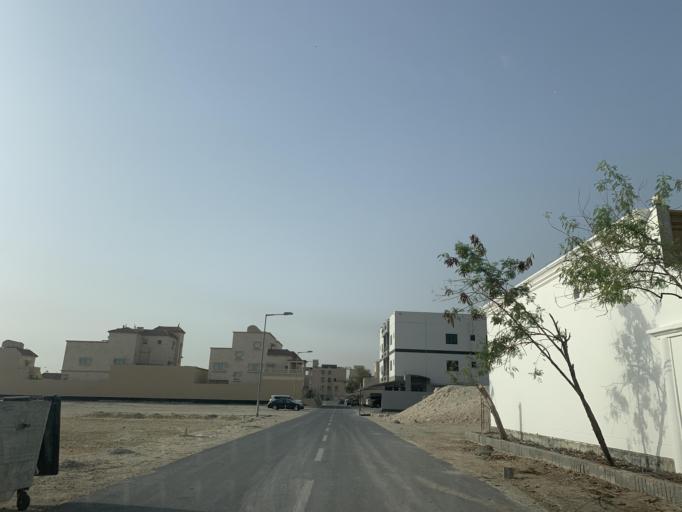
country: BH
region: Northern
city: Madinat `Isa
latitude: 26.1929
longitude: 50.5655
